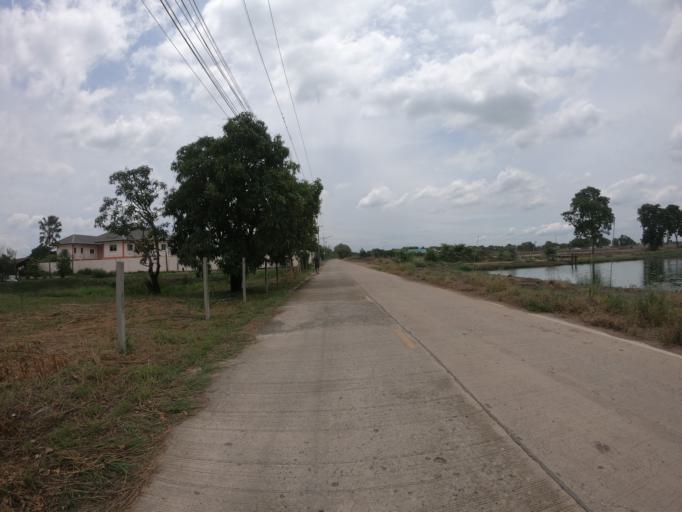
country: TH
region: Pathum Thani
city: Ban Lam Luk Ka
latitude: 13.9779
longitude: 100.8541
